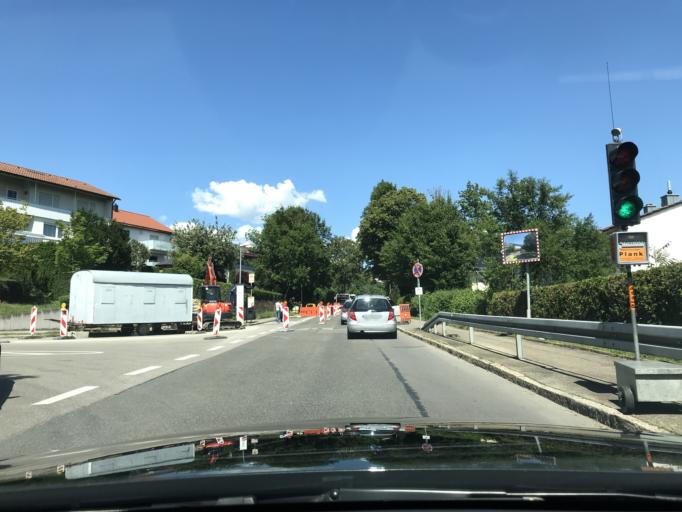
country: DE
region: Baden-Wuerttemberg
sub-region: Regierungsbezirk Stuttgart
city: Waiblingen
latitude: 48.8331
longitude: 9.3300
